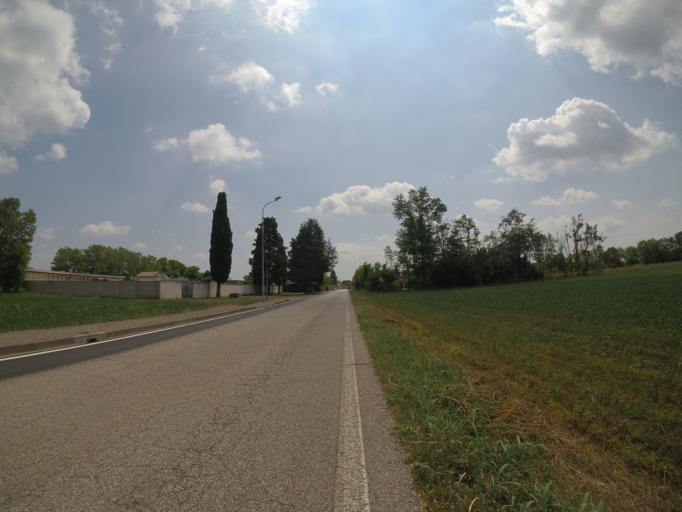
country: IT
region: Friuli Venezia Giulia
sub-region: Provincia di Udine
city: Basiliano
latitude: 45.9991
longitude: 13.0769
